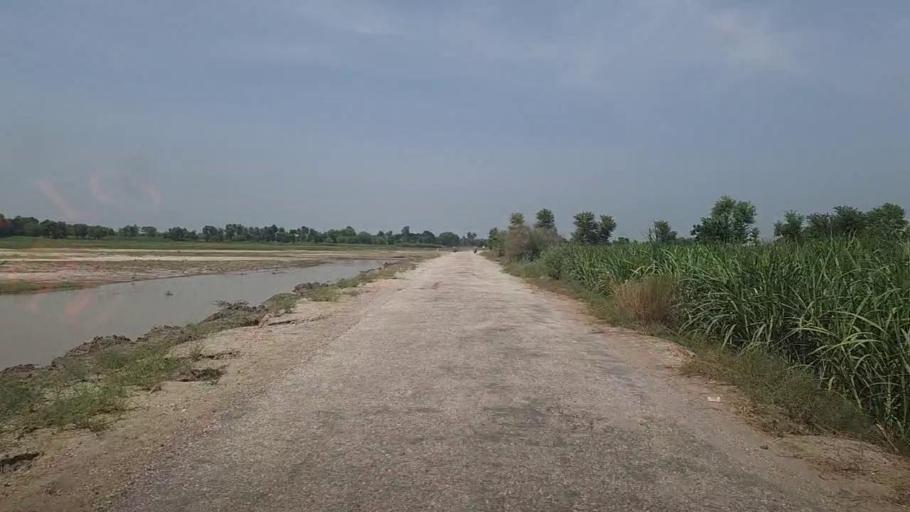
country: PK
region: Sindh
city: Ubauro
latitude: 28.1852
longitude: 69.7694
